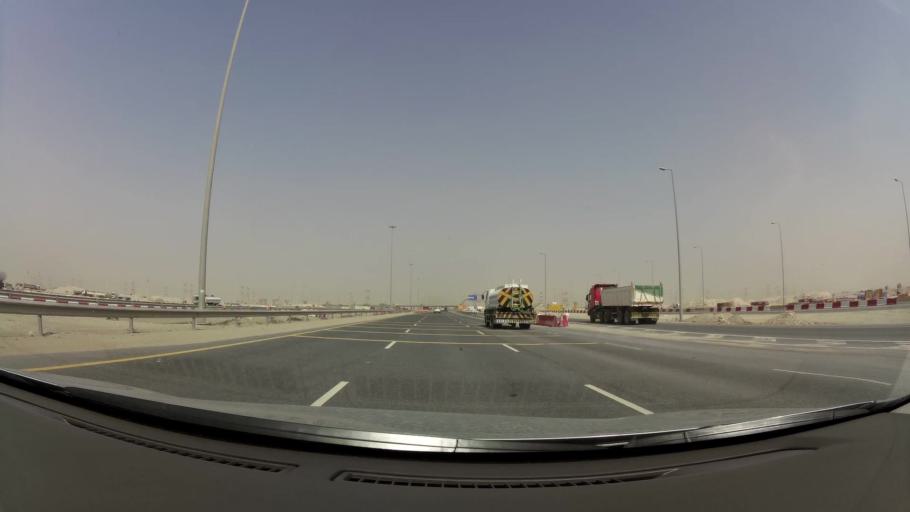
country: QA
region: Baladiyat ar Rayyan
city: Ar Rayyan
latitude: 25.1697
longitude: 51.3197
